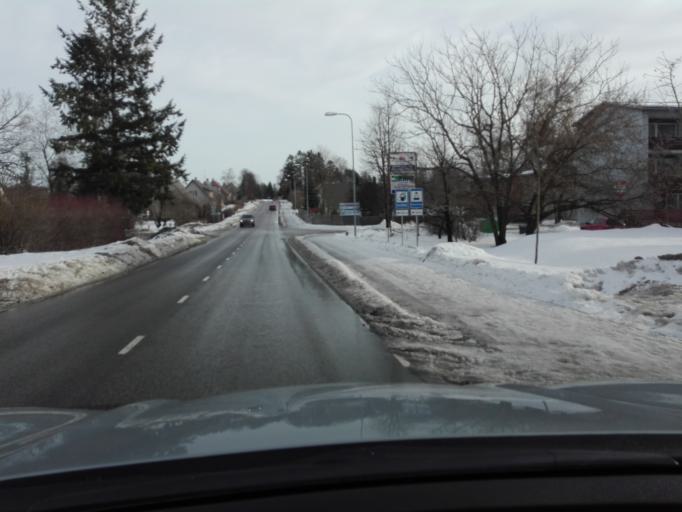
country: EE
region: Raplamaa
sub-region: Rapla vald
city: Rapla
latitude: 59.0003
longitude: 24.7980
